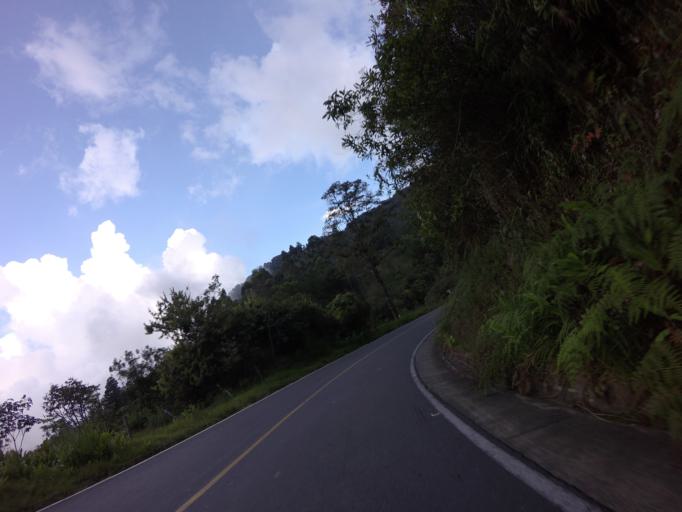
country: CO
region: Caldas
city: Pensilvania
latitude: 5.3754
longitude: -75.1496
